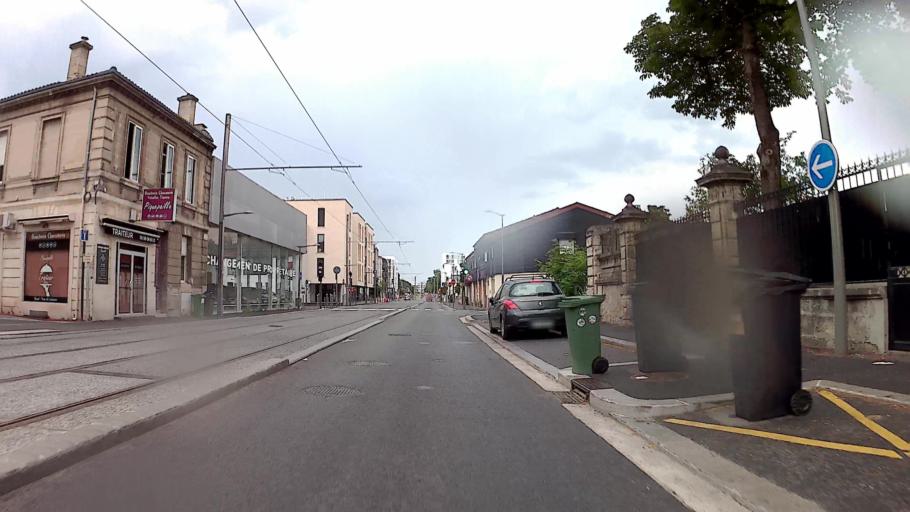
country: FR
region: Aquitaine
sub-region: Departement de la Gironde
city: Le Bouscat
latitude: 44.8633
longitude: -0.6030
